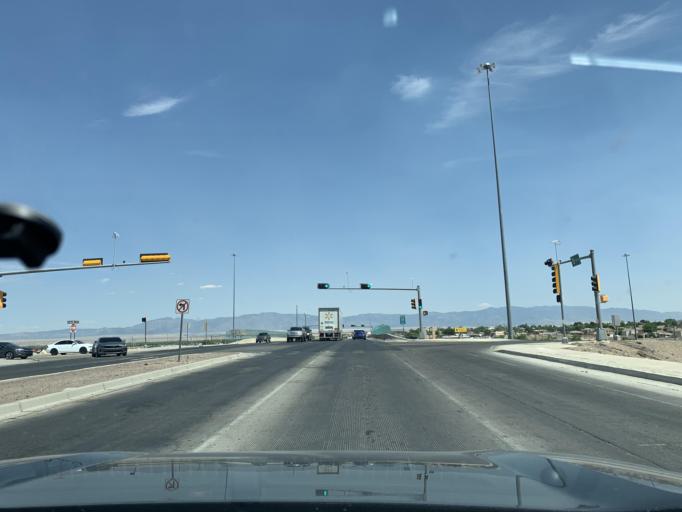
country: US
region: New Mexico
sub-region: Valencia County
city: Los Lunas
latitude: 34.8148
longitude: -106.7626
